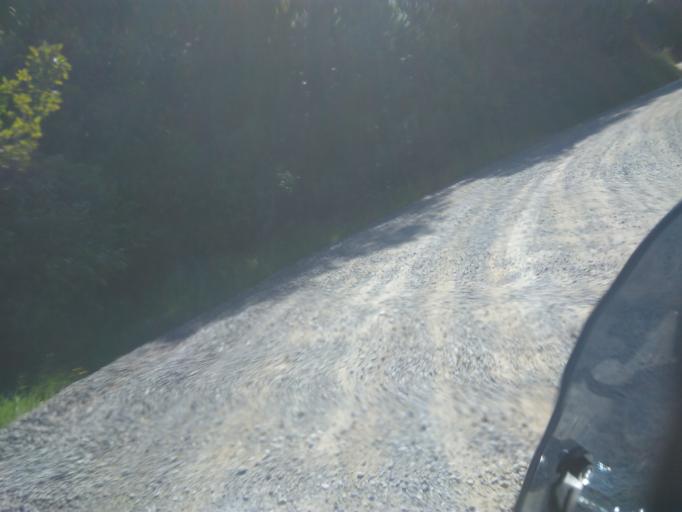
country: NZ
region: Hawke's Bay
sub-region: Wairoa District
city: Wairoa
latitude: -38.7974
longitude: 177.1244
